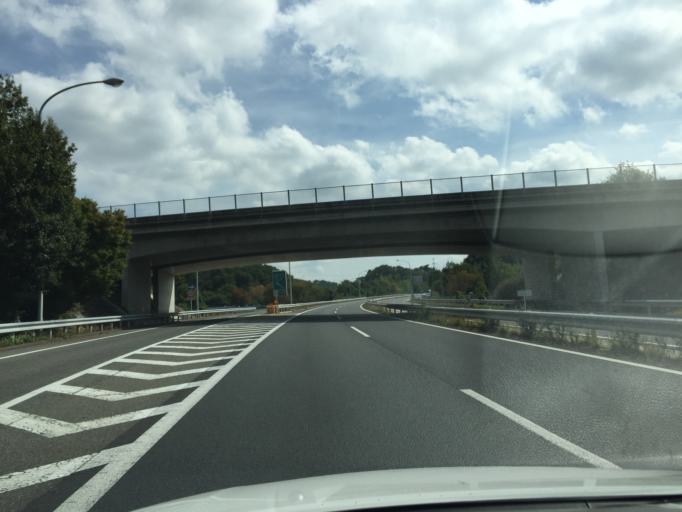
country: JP
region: Fukushima
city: Miharu
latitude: 37.4428
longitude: 140.4398
